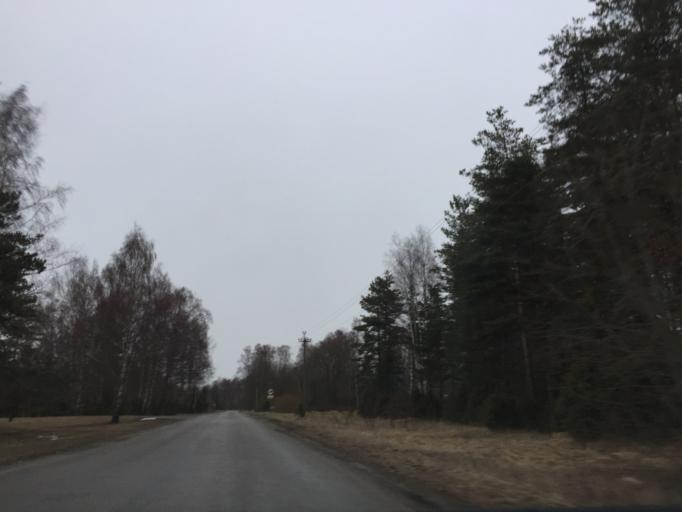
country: EE
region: Laeaene
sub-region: Lihula vald
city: Lihula
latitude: 58.6255
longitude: 23.6326
